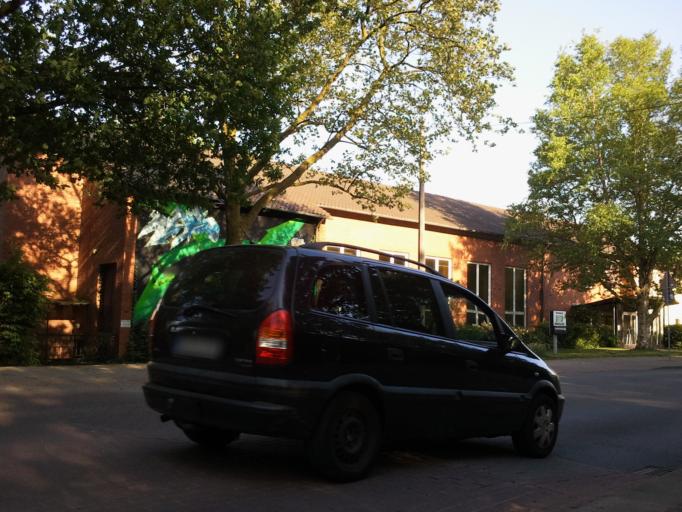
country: DE
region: Lower Saxony
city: Nienburg
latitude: 52.6390
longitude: 9.2149
